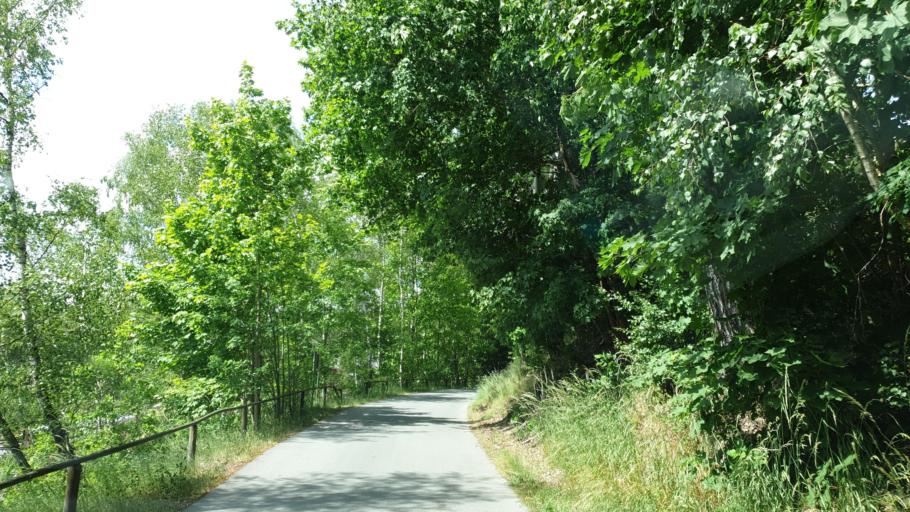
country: DE
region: Saxony
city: Adorf
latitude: 50.3328
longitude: 12.2580
